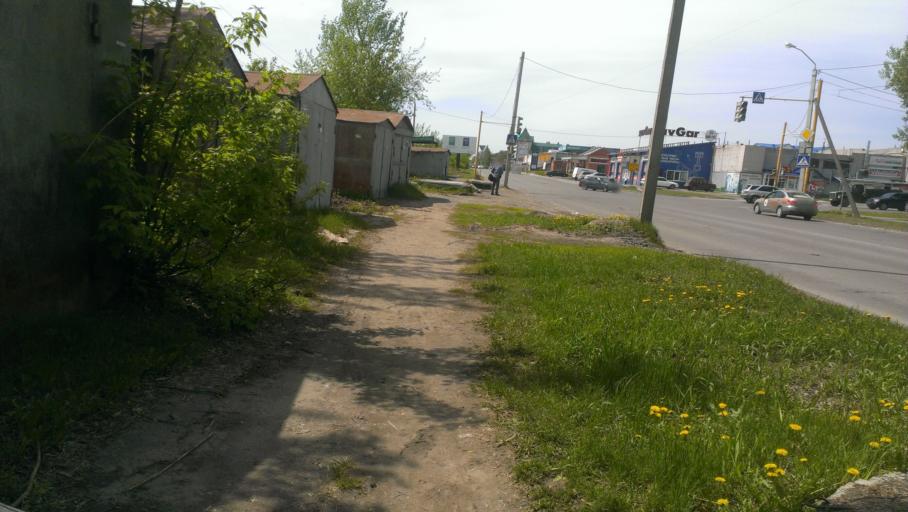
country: RU
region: Altai Krai
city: Novosilikatnyy
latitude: 53.3569
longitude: 83.6597
